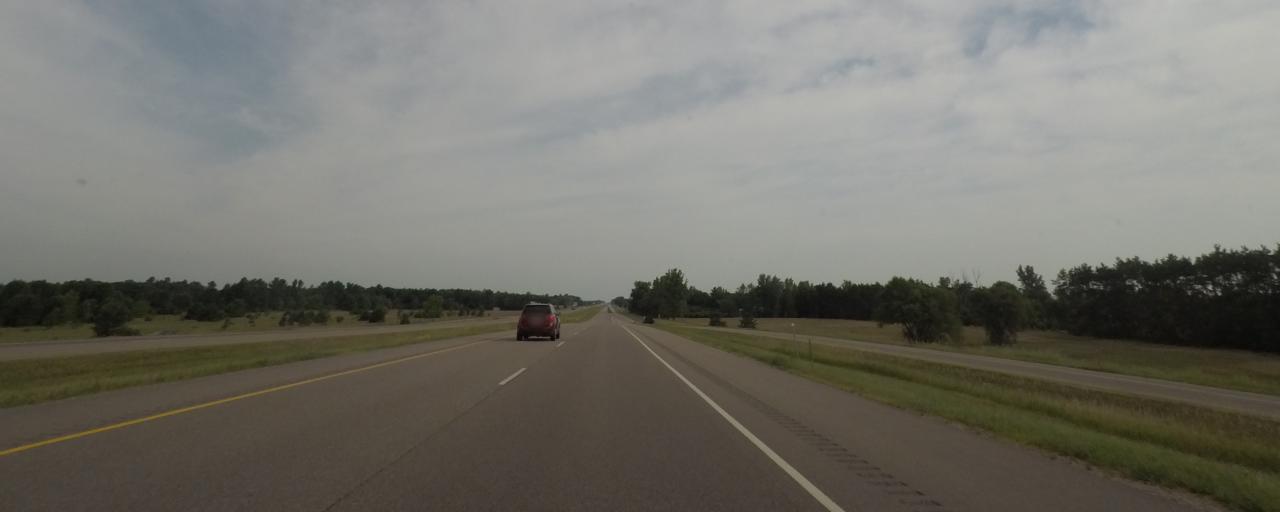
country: US
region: Wisconsin
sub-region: Portage County
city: Plover
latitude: 44.2153
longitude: -89.5244
